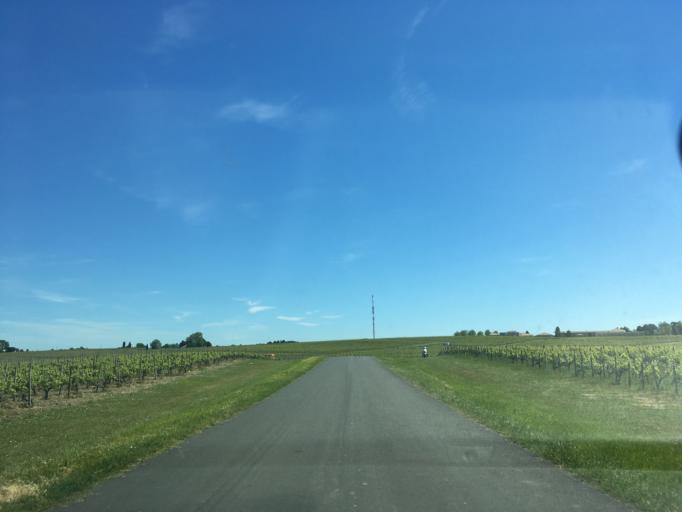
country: FR
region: Aquitaine
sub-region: Departement de la Gironde
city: Lesparre-Medoc
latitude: 45.3152
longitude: -0.8813
